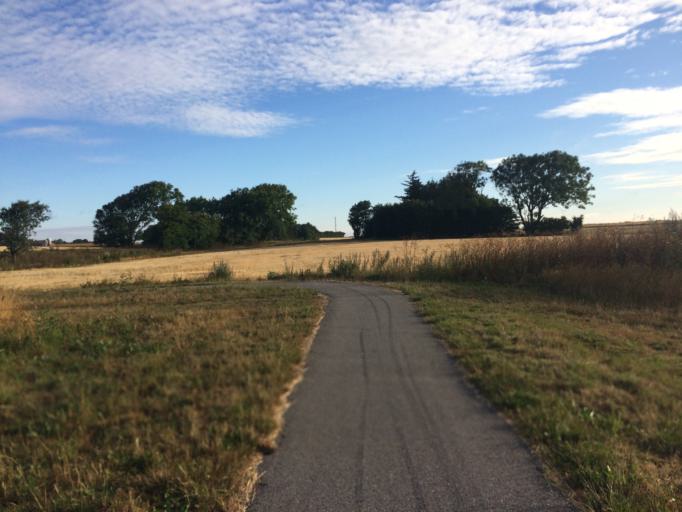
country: DK
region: Central Jutland
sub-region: Holstebro Kommune
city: Vinderup
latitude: 56.6035
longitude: 8.8661
